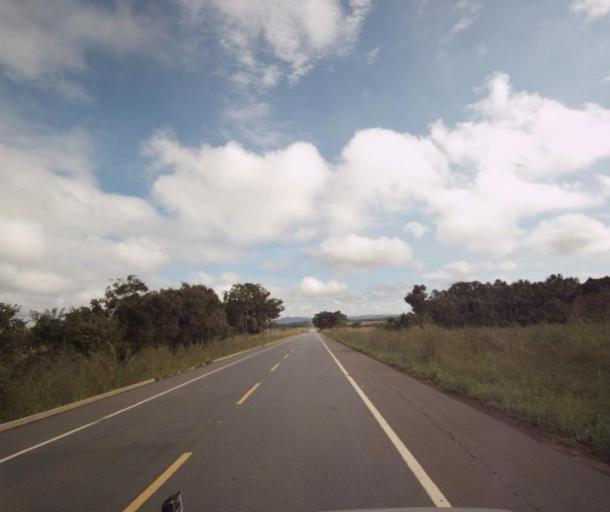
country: BR
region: Goias
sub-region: Barro Alto
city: Barro Alto
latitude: -15.2478
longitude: -48.6894
